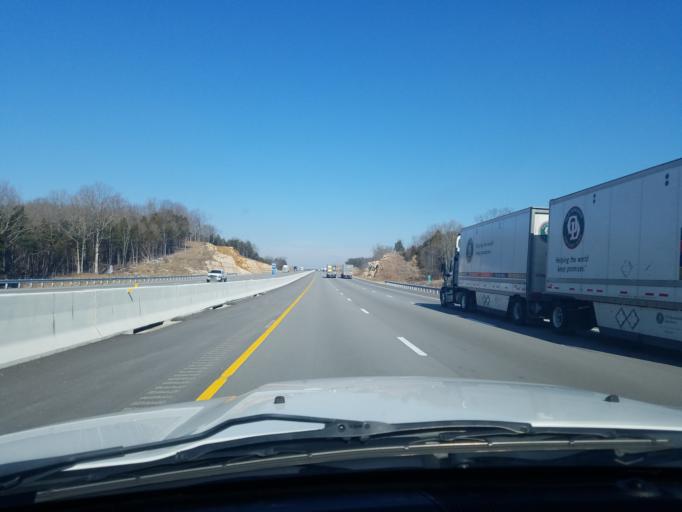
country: US
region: Kentucky
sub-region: Hart County
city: Munfordville
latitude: 37.4157
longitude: -85.8818
